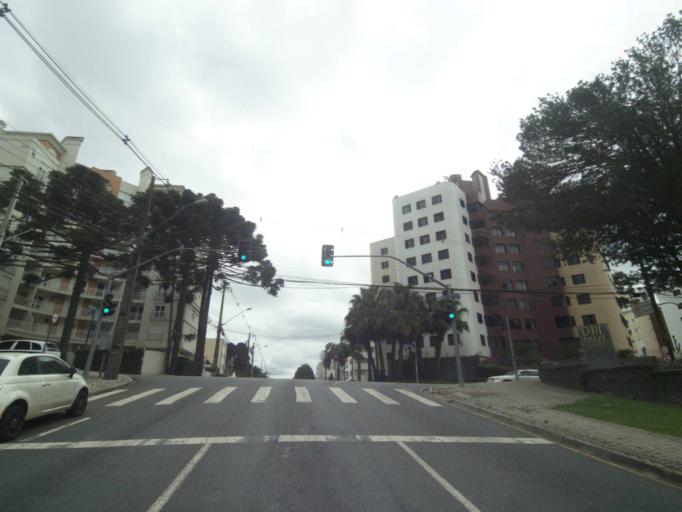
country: BR
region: Parana
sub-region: Curitiba
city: Curitiba
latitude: -25.4348
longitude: -49.2976
